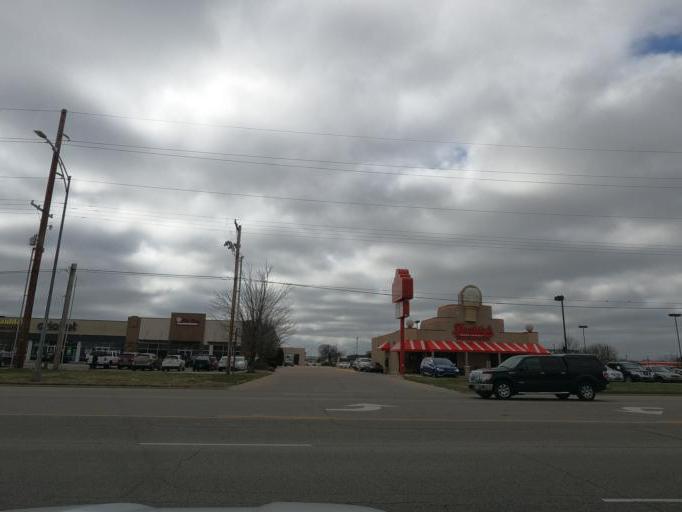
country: US
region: Kansas
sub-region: Reno County
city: Hutchinson
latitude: 38.0724
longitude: -97.9015
